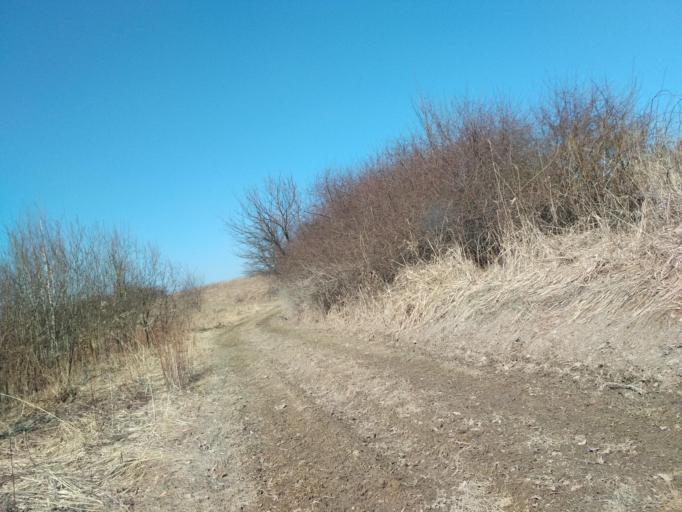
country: PL
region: Subcarpathian Voivodeship
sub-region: Powiat brzozowski
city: Golcowa
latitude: 49.7633
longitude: 22.0309
